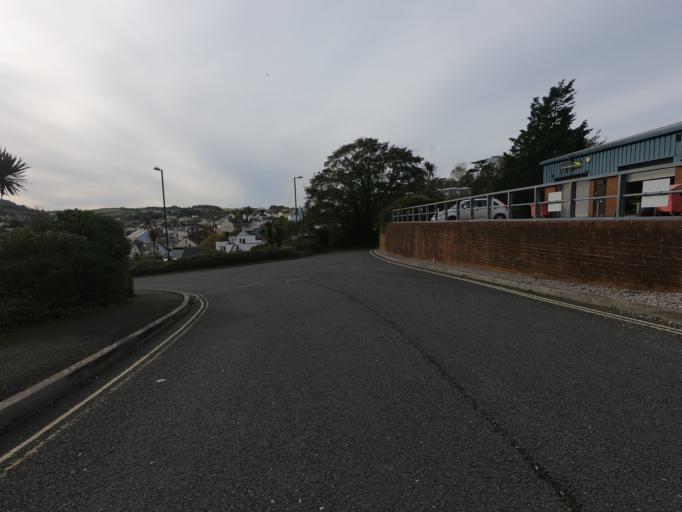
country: GB
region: England
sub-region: Borough of Torbay
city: Brixham
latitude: 50.3905
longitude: -3.5134
